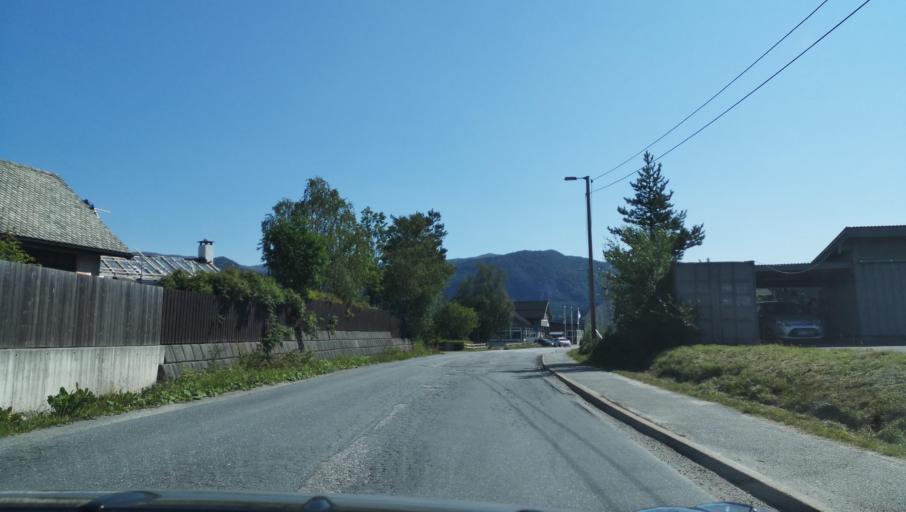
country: NO
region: Hordaland
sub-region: Voss
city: Voss
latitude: 60.6346
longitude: 6.4620
